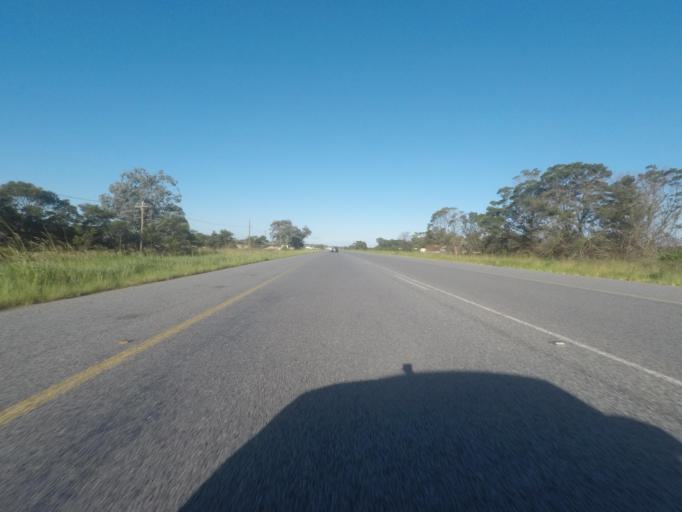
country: ZA
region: Eastern Cape
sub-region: Buffalo City Metropolitan Municipality
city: East London
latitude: -33.0567
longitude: 27.7986
